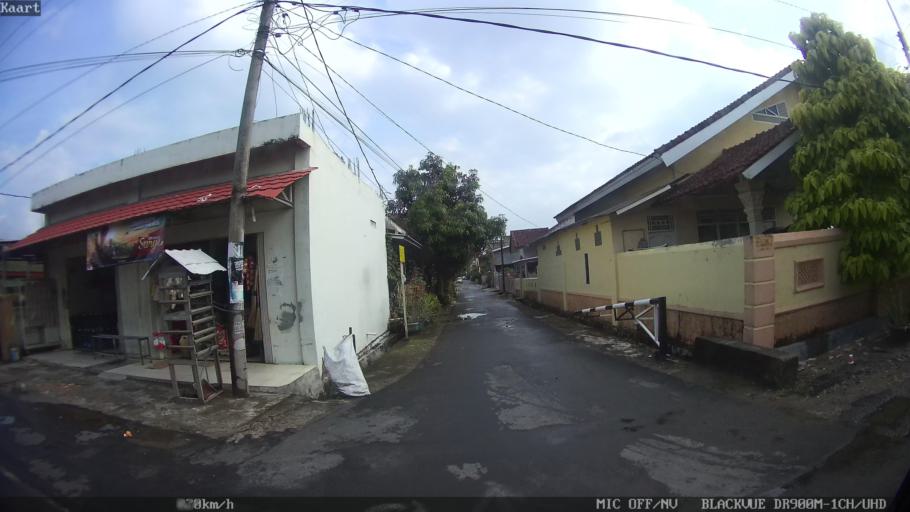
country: ID
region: Lampung
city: Kedaton
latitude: -5.3910
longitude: 105.3062
